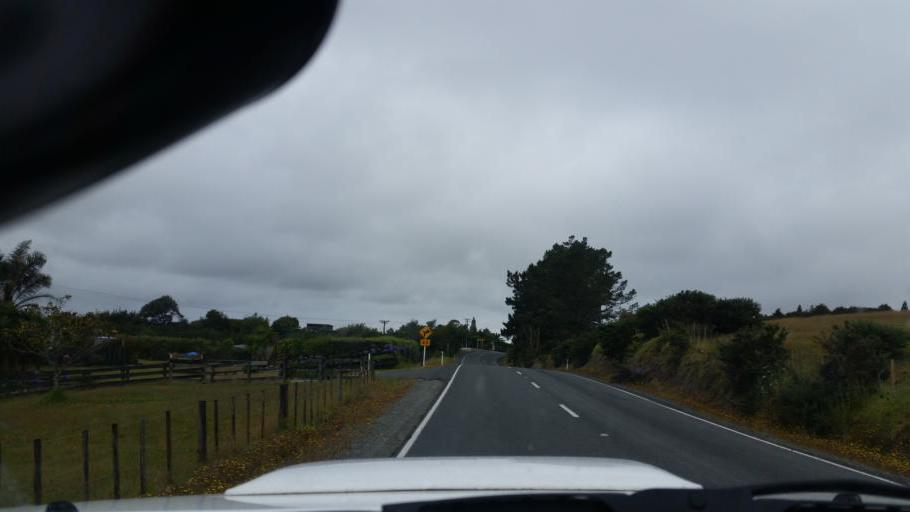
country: NZ
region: Auckland
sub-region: Auckland
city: Wellsford
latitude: -36.1334
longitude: 174.5376
